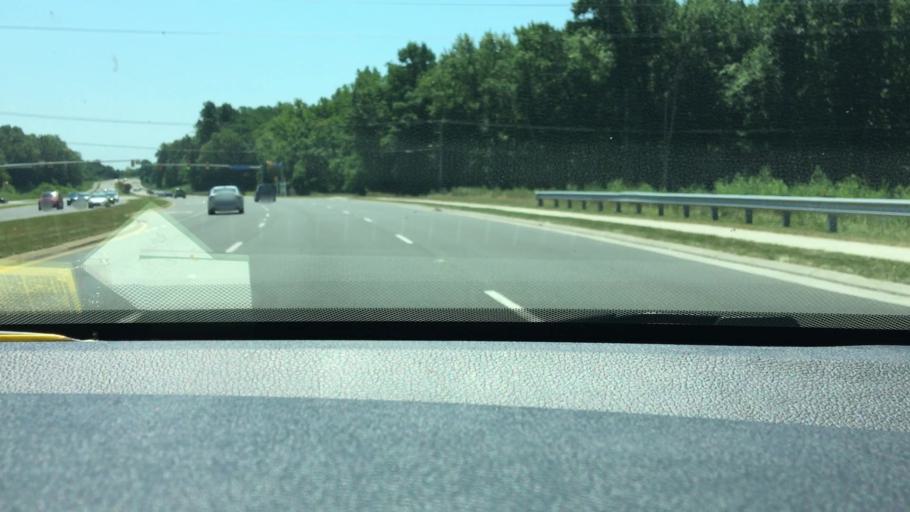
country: US
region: Virginia
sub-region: Prince William County
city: Dale City
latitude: 38.6610
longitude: -77.3260
